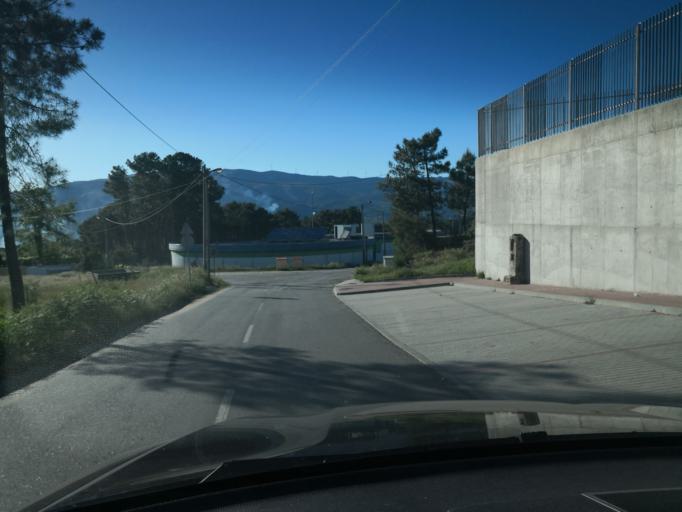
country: PT
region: Vila Real
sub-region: Vila Real
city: Vila Real
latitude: 41.3152
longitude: -7.6963
